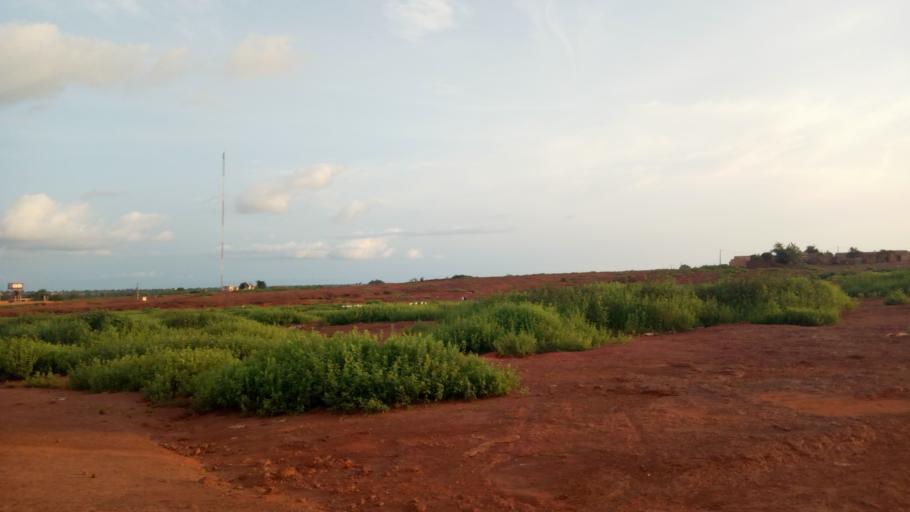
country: ML
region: Sikasso
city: Koutiala
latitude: 12.3751
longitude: -5.4789
